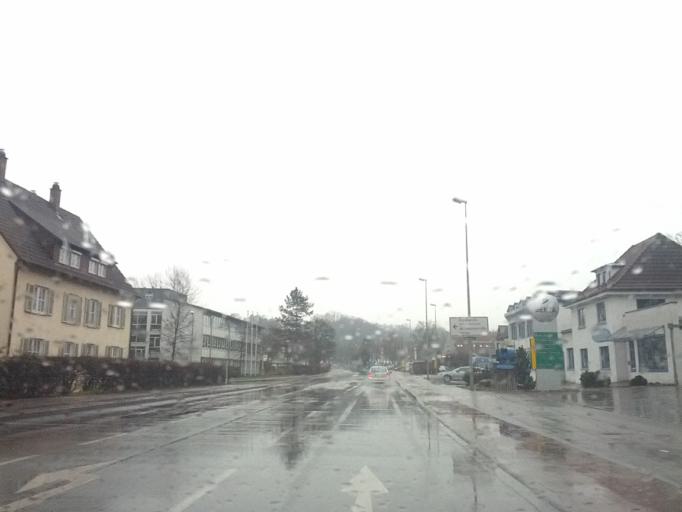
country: DE
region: Baden-Wuerttemberg
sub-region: Tuebingen Region
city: Biberach an der Riss
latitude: 48.0887
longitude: 9.7939
